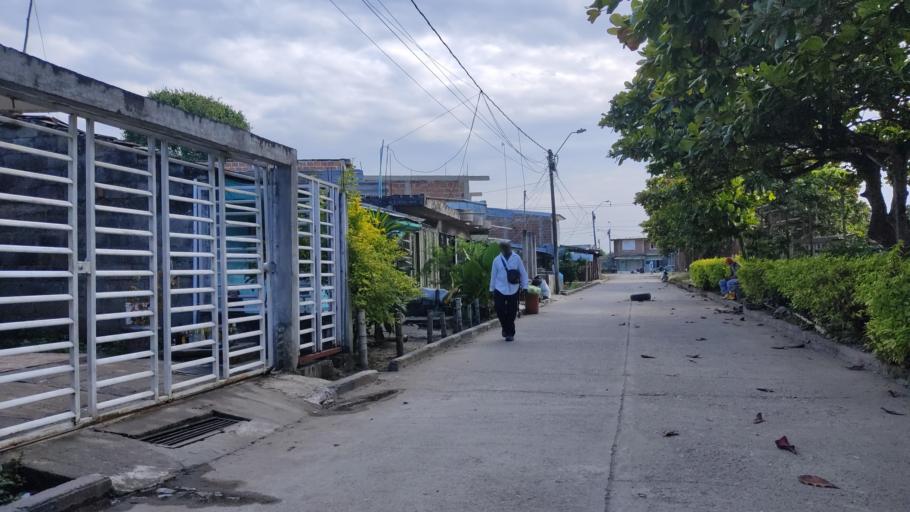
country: CO
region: Valle del Cauca
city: Jamundi
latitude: 3.1279
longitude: -76.5566
